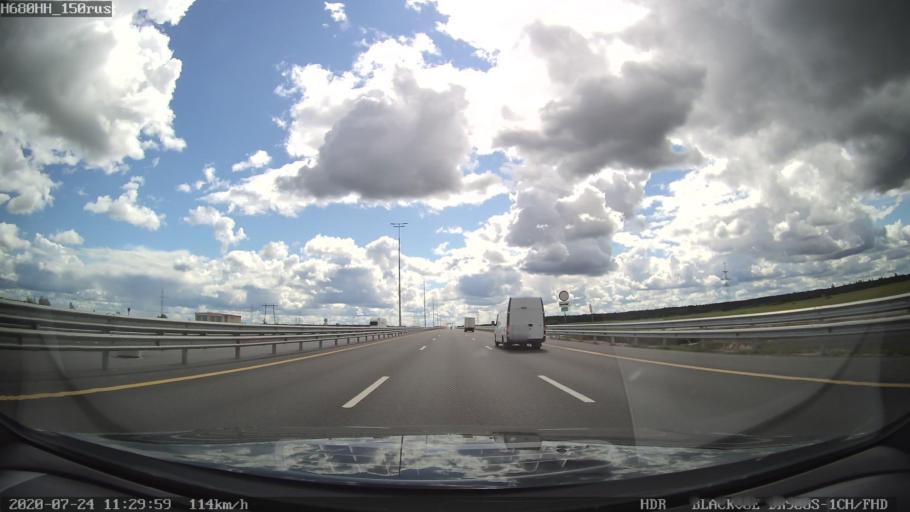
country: RU
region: Leningrad
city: Krasnyy Bor
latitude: 59.6752
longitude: 30.6022
